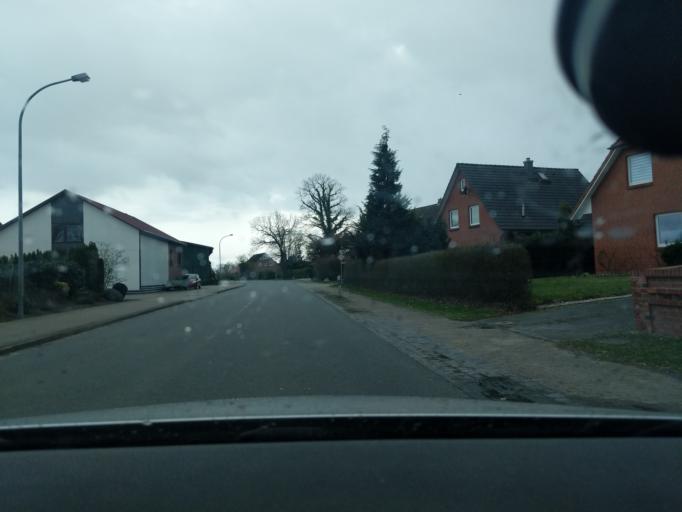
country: DE
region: Lower Saxony
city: Bargstedt
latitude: 53.4678
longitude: 9.4729
